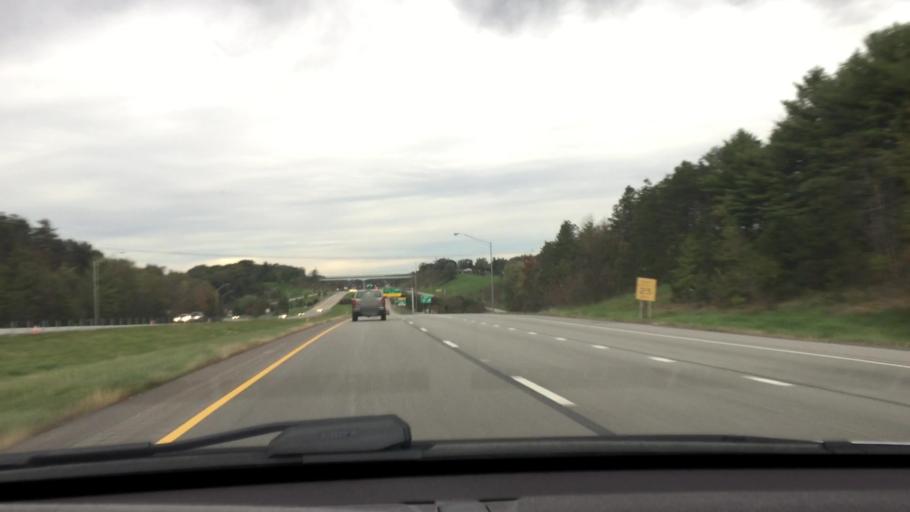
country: US
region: Pennsylvania
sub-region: Beaver County
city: West Mayfield
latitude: 40.7585
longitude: -80.3648
